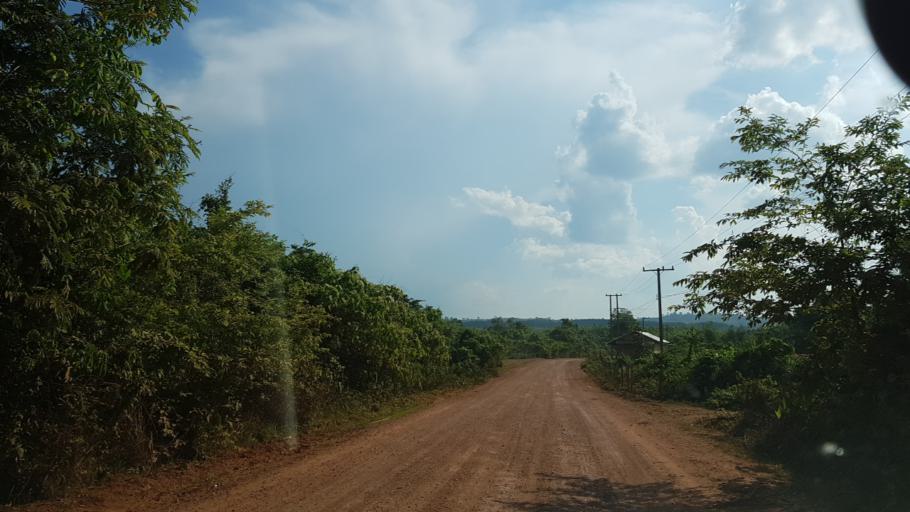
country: LA
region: Vientiane
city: Muang Phon-Hong
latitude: 18.3451
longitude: 102.2998
